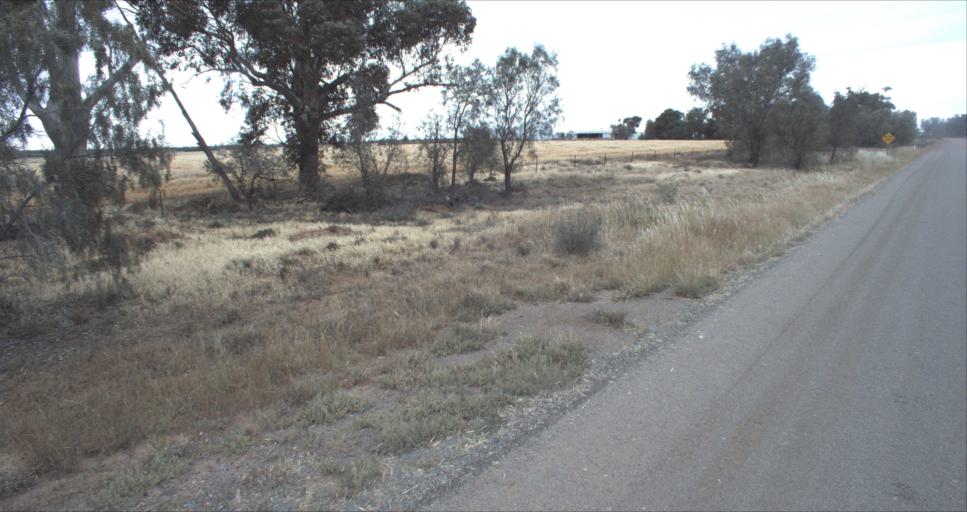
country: AU
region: New South Wales
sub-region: Leeton
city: Leeton
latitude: -34.4437
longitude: 146.3753
